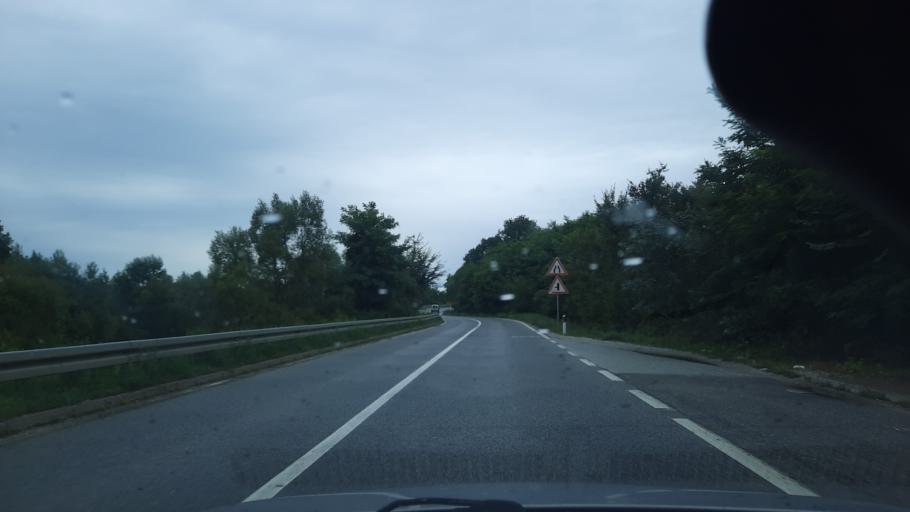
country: RS
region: Central Serbia
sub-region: Sumadijski Okrug
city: Knic
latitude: 43.8306
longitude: 20.7818
